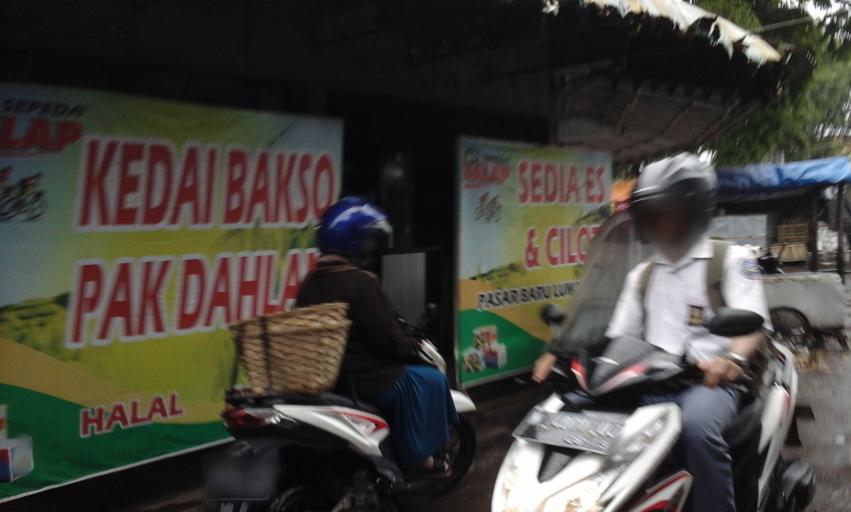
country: ID
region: East Java
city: Rogotrunan
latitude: -8.1246
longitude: 113.2249
